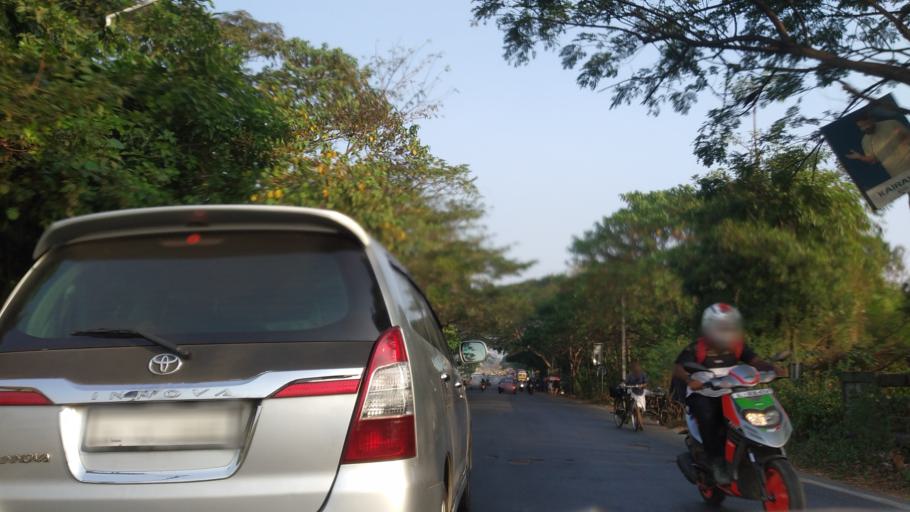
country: IN
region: Kerala
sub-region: Thrissur District
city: Kodungallur
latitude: 10.2006
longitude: 76.2005
